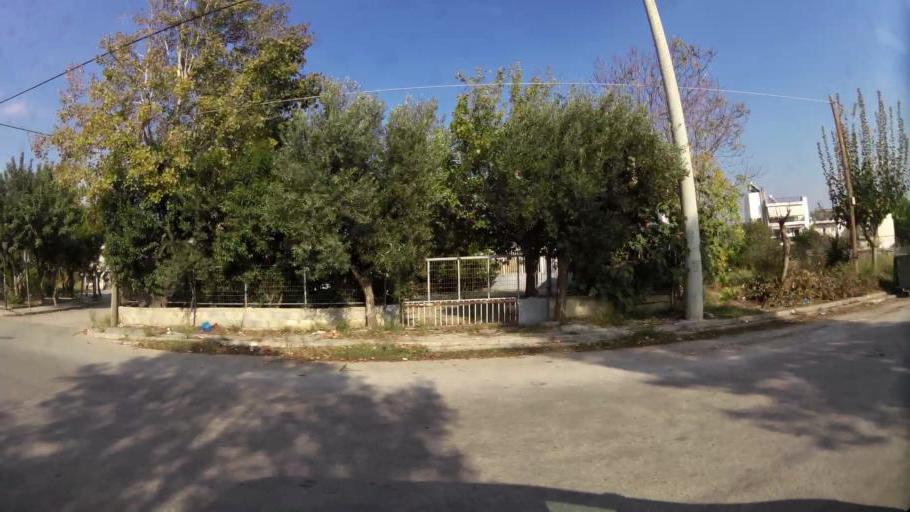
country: GR
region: Attica
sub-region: Nomarchia Anatolikis Attikis
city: Acharnes
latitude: 38.0765
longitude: 23.7281
